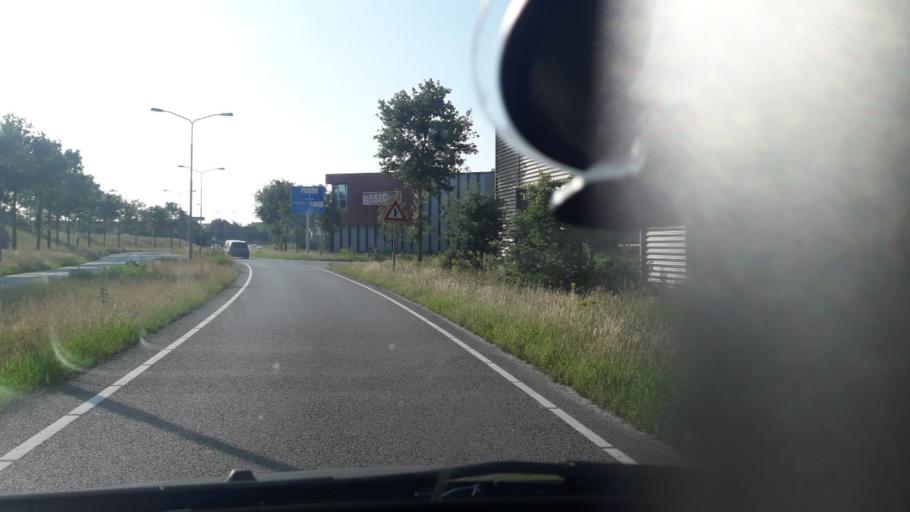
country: NL
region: Gelderland
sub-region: Gemeente Harderwijk
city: Harderwijk
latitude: 52.3217
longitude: 5.6127
